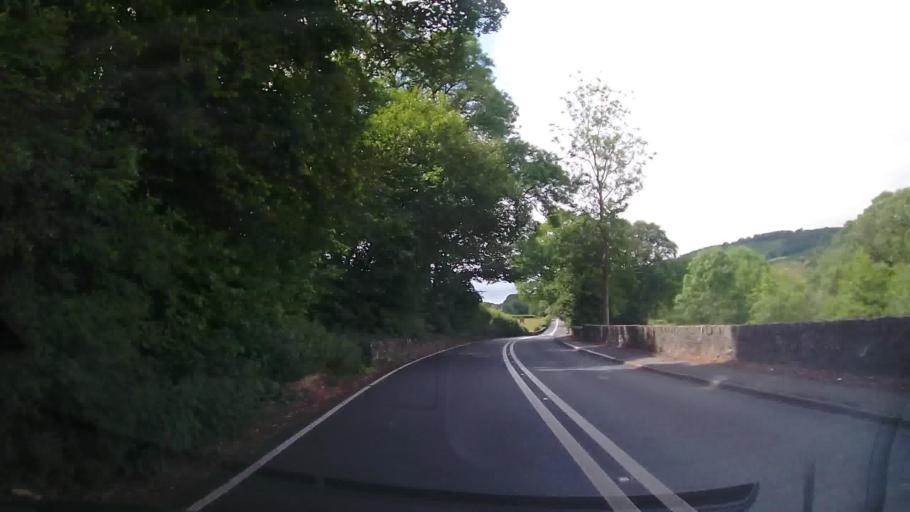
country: GB
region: Wales
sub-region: Denbighshire
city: Corwen
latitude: 52.9766
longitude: -3.3314
